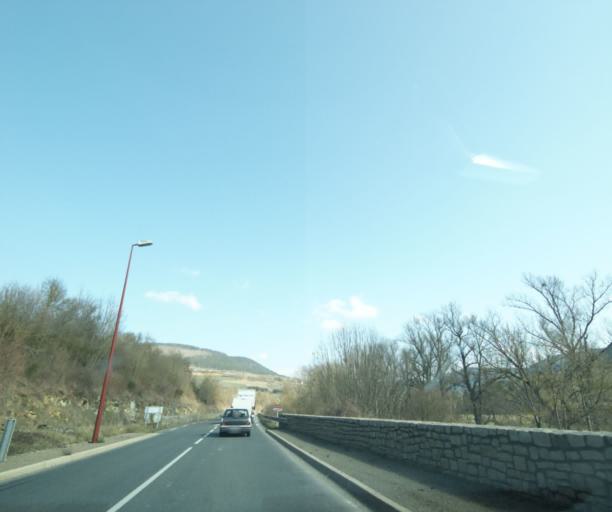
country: FR
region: Languedoc-Roussillon
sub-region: Departement de la Lozere
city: Chanac
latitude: 44.4838
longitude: 3.3621
